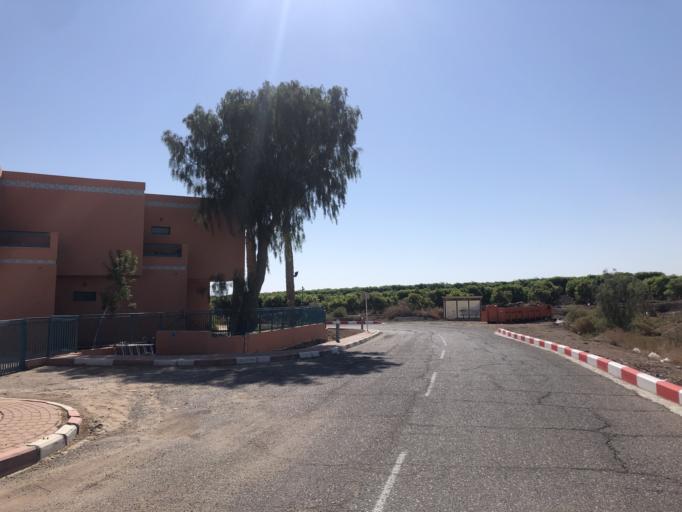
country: IL
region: Southern District
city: Eilat
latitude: 29.5801
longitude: 34.9610
